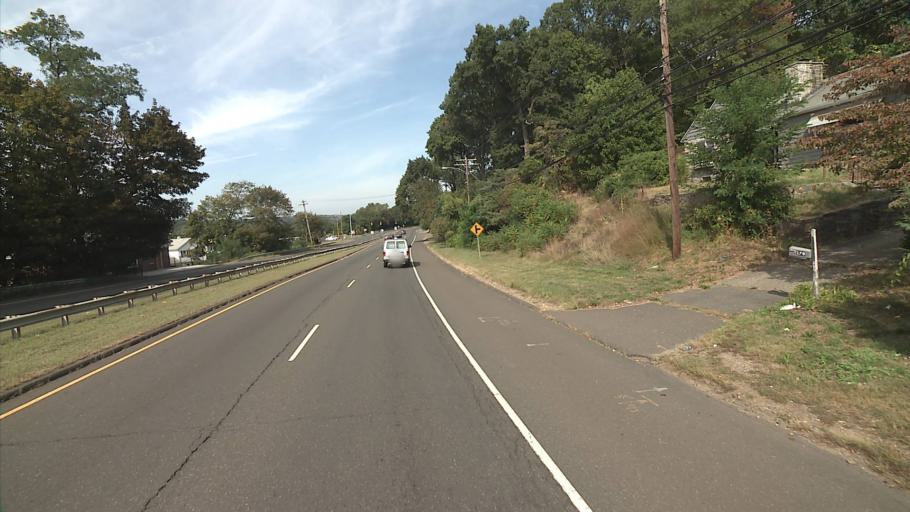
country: US
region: Connecticut
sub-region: New Haven County
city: Derby
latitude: 41.3082
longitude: -73.0719
